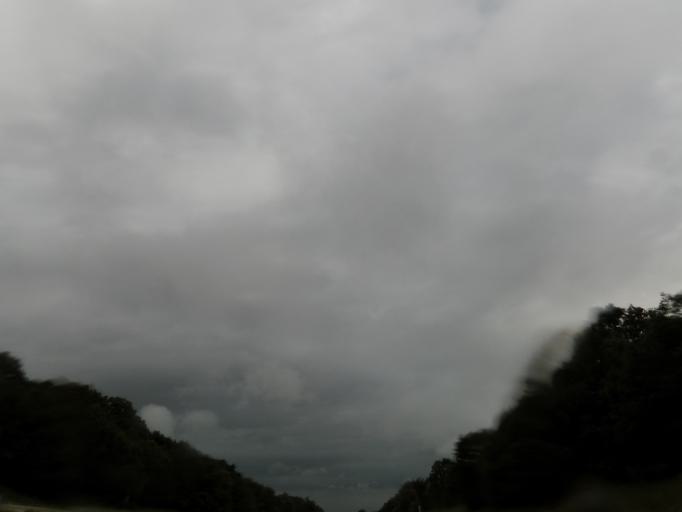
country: US
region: Illinois
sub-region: Clinton County
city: Wamac
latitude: 38.3811
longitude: -89.1145
